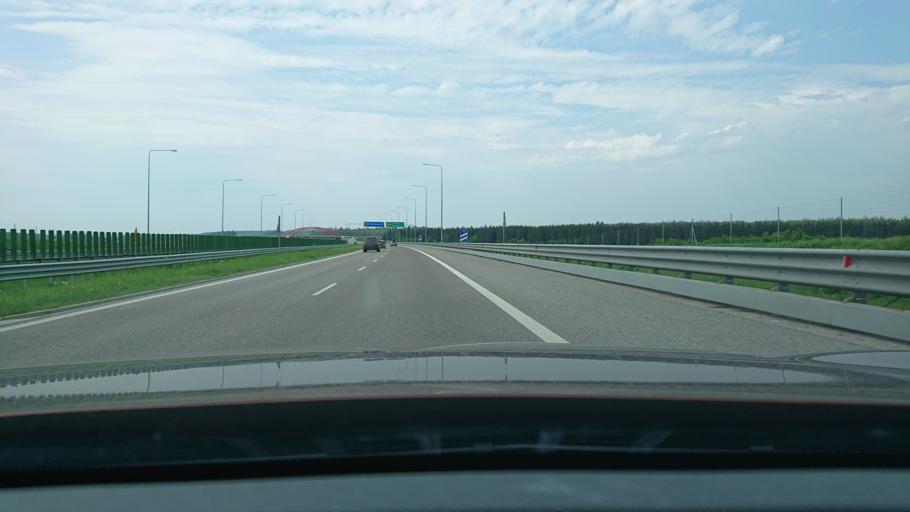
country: PL
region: Subcarpathian Voivodeship
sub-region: Powiat jaroslawski
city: Pawlosiow
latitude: 49.9674
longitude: 22.6534
